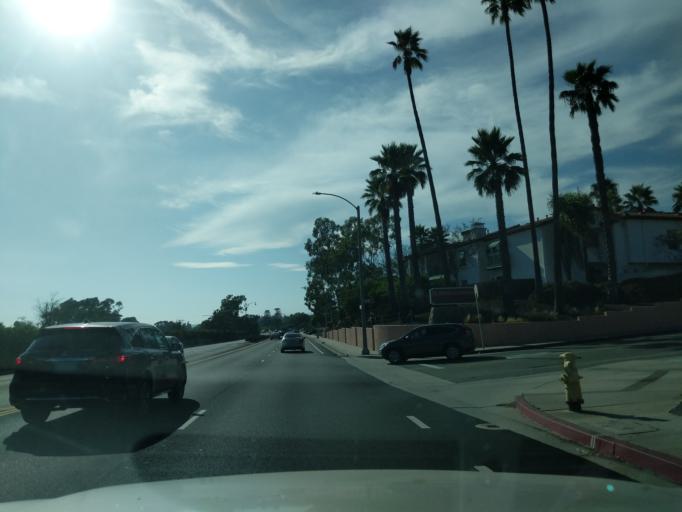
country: US
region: California
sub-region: Santa Barbara County
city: Mission Canyon
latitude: 34.4412
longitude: -119.7565
